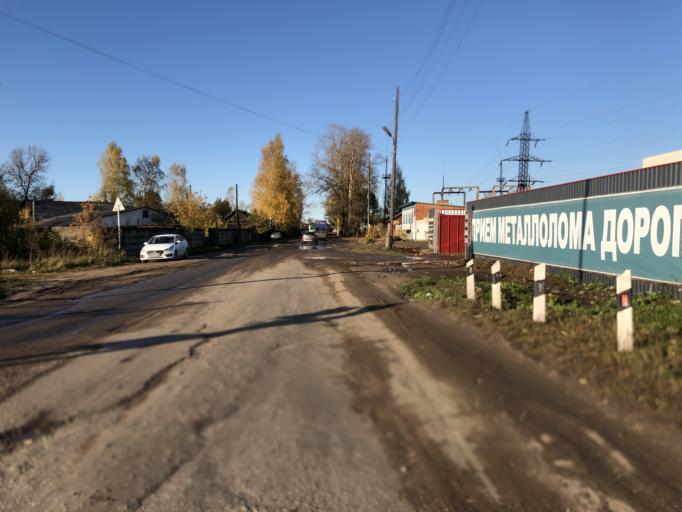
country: RU
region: Tverskaya
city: Rzhev
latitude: 56.2385
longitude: 34.3461
